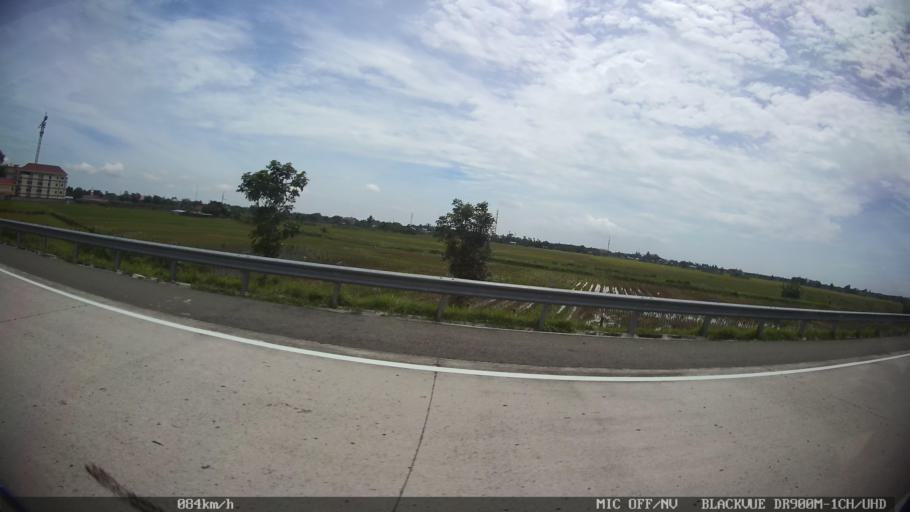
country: ID
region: North Sumatra
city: Percut
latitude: 3.5475
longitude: 98.8532
